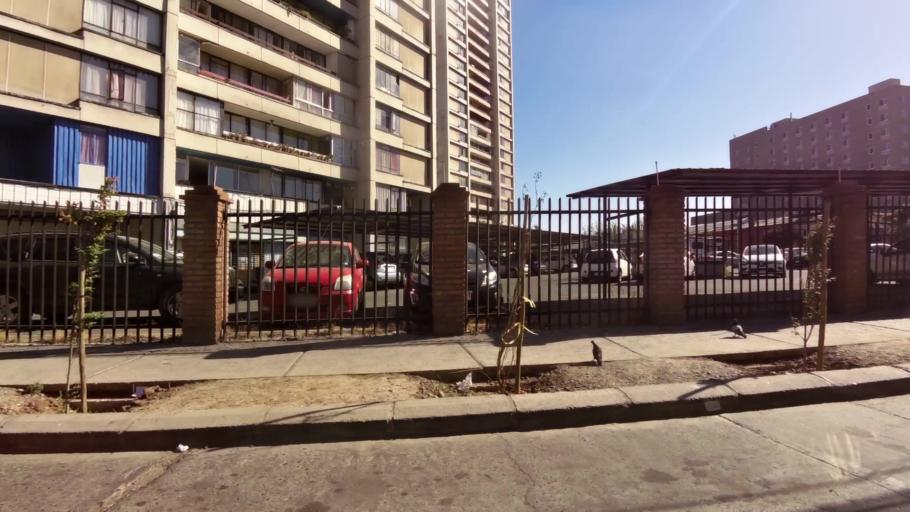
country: CL
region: O'Higgins
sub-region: Provincia de Cachapoal
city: Rancagua
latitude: -34.1674
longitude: -70.7361
